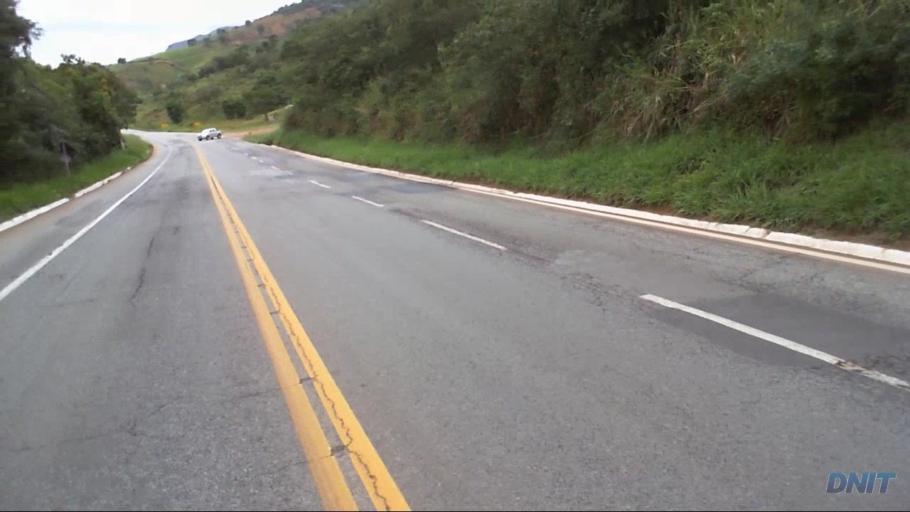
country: BR
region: Minas Gerais
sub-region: Barao De Cocais
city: Barao de Cocais
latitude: -19.8228
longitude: -43.3869
